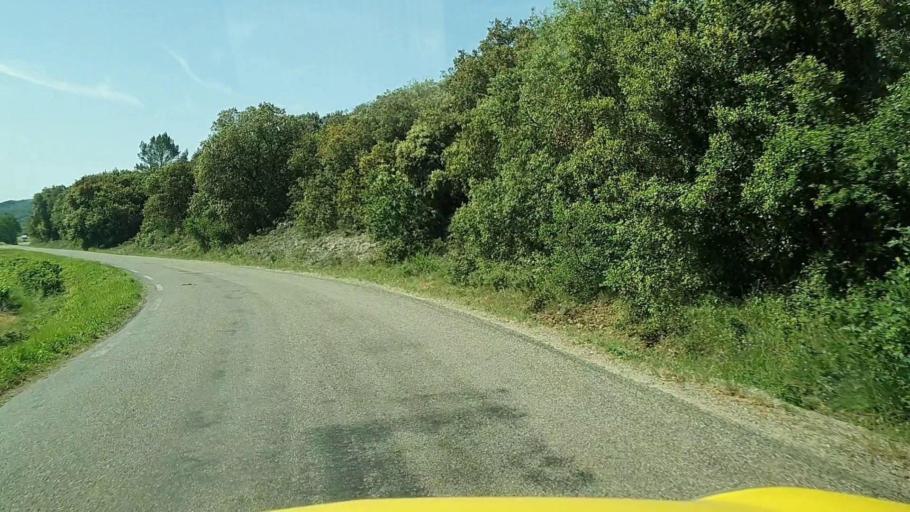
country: FR
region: Languedoc-Roussillon
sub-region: Departement du Gard
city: Sabran
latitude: 44.1238
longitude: 4.5011
